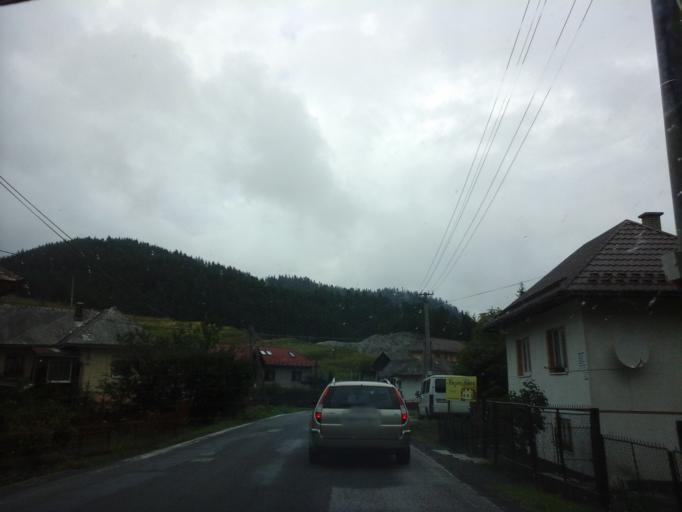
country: SK
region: Kosicky
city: Dobsina
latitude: 48.9164
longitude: 20.2647
